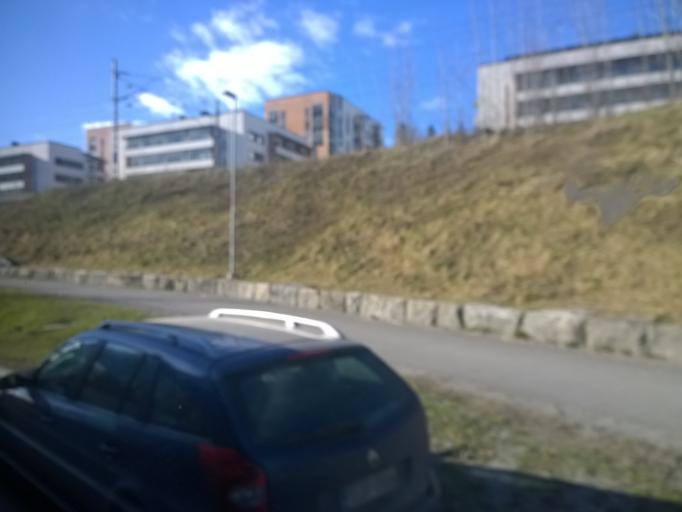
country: FI
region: Pirkanmaa
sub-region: Tampere
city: Tampere
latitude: 61.4912
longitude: 23.7910
